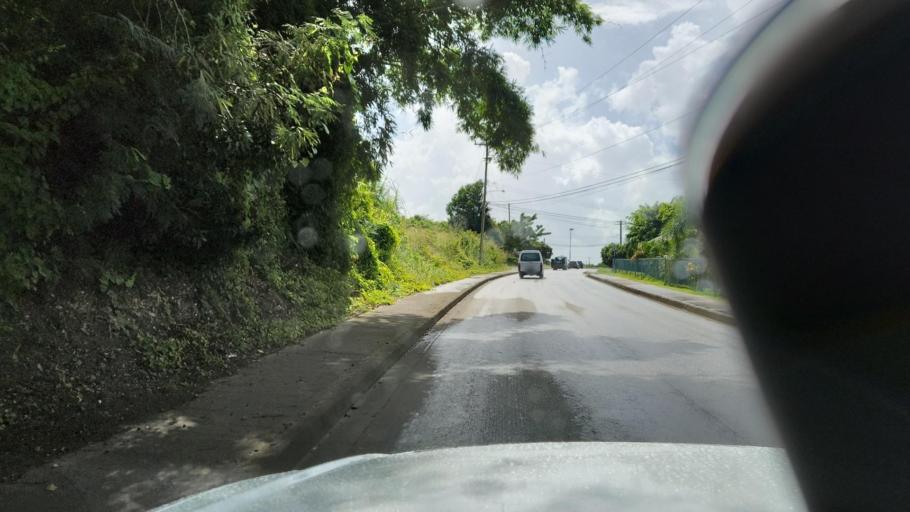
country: BB
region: Saint Michael
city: Bridgetown
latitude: 13.1084
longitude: -59.5681
